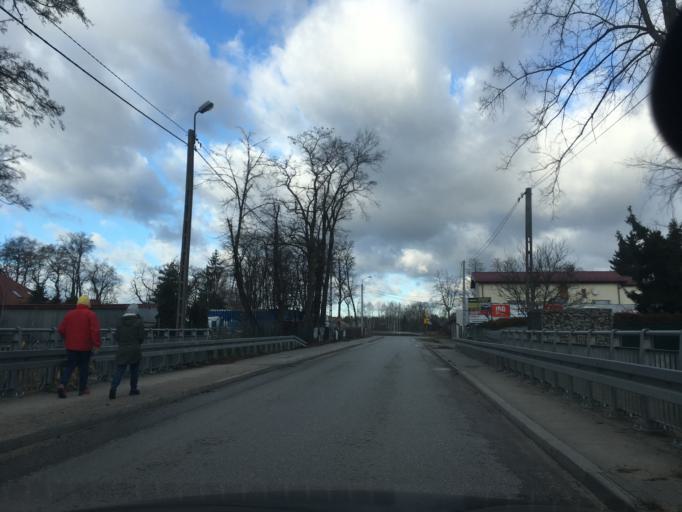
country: PL
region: Masovian Voivodeship
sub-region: Powiat piaseczynski
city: Lesznowola
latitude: 52.0385
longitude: 20.9445
